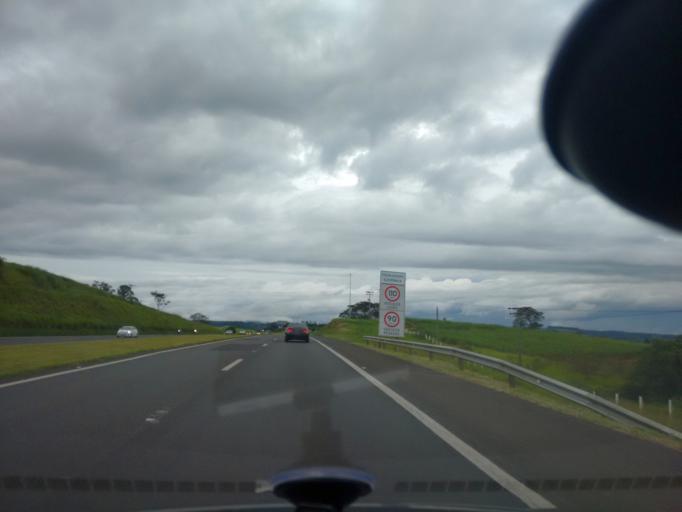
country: BR
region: Sao Paulo
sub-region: Rio Claro
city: Rio Claro
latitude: -22.3436
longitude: -47.6514
